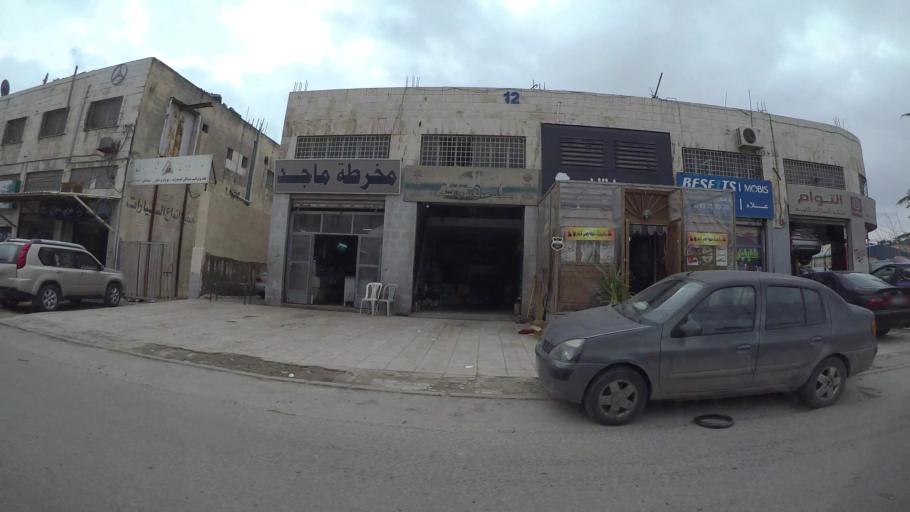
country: JO
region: Amman
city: Wadi as Sir
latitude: 31.9447
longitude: 35.8406
